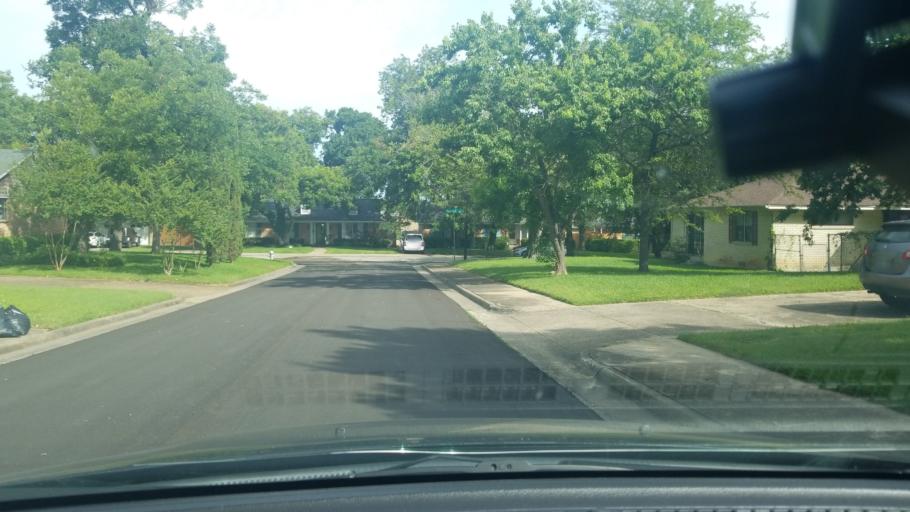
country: US
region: Texas
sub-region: Dallas County
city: Highland Park
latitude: 32.8099
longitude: -96.6998
